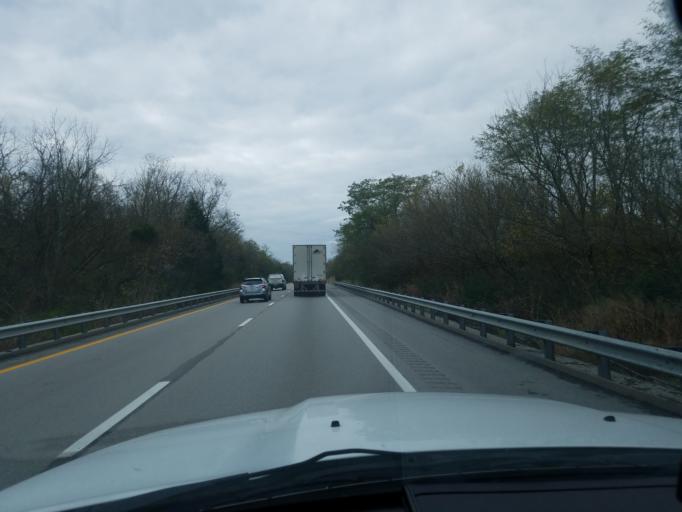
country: US
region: Kentucky
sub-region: Henry County
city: New Castle
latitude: 38.4701
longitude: -85.2799
